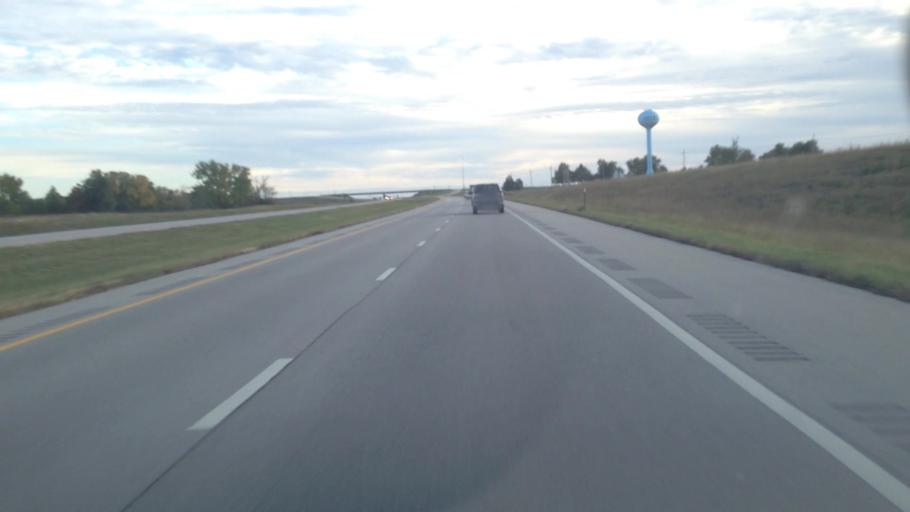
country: US
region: Kansas
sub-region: Douglas County
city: Baldwin City
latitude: 38.8429
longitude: -95.2679
